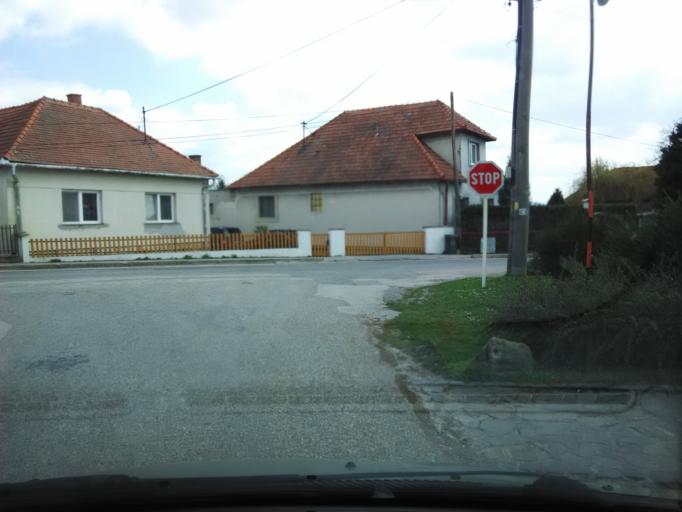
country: SK
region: Nitriansky
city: Zlate Moravce
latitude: 48.4426
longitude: 18.3620
